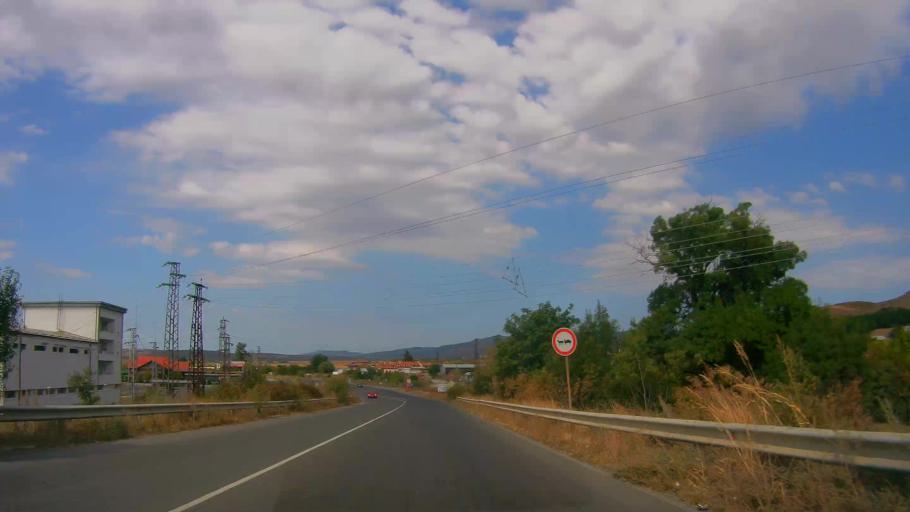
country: BG
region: Burgas
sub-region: Obshtina Aytos
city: Aytos
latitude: 42.7049
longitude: 27.2386
